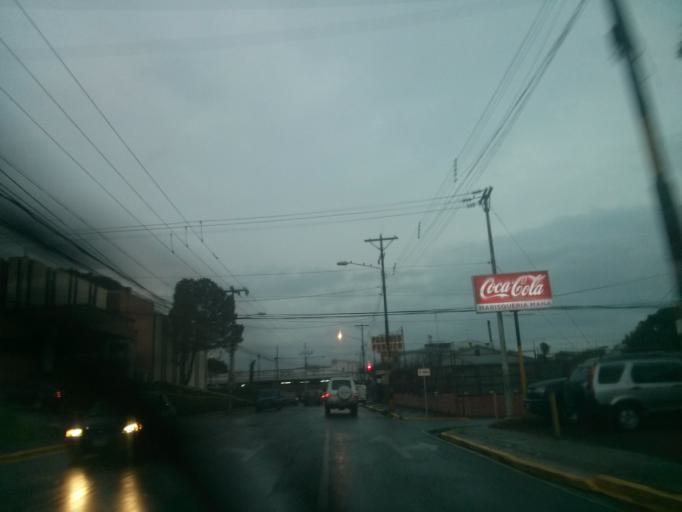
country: CR
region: Alajuela
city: Alajuela
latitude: 10.0213
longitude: -84.2157
